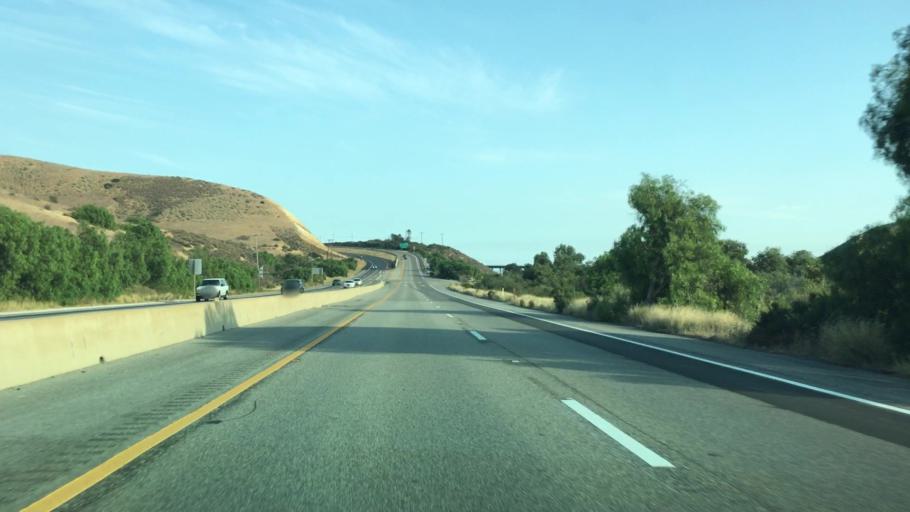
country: US
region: California
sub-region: Santa Barbara County
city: Buellton
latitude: 34.4799
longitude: -120.2294
